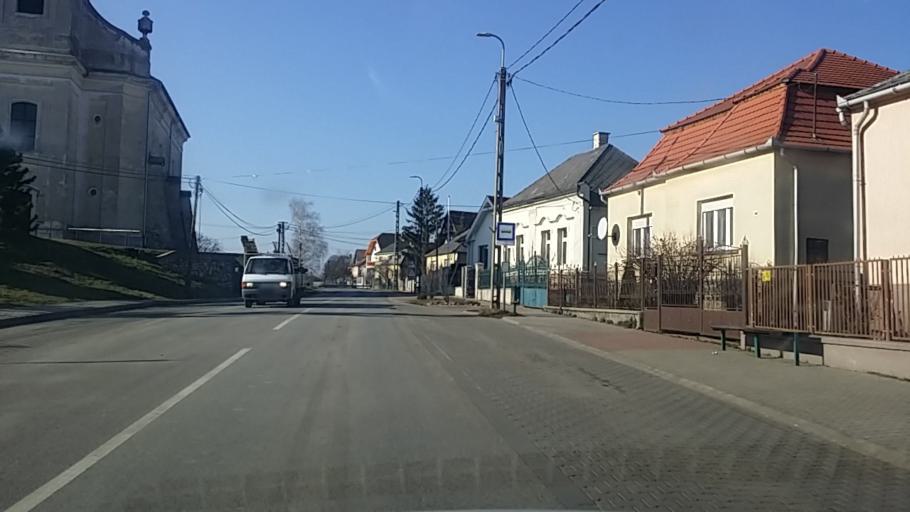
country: HU
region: Komarom-Esztergom
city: Bokod
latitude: 47.5191
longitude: 18.2268
